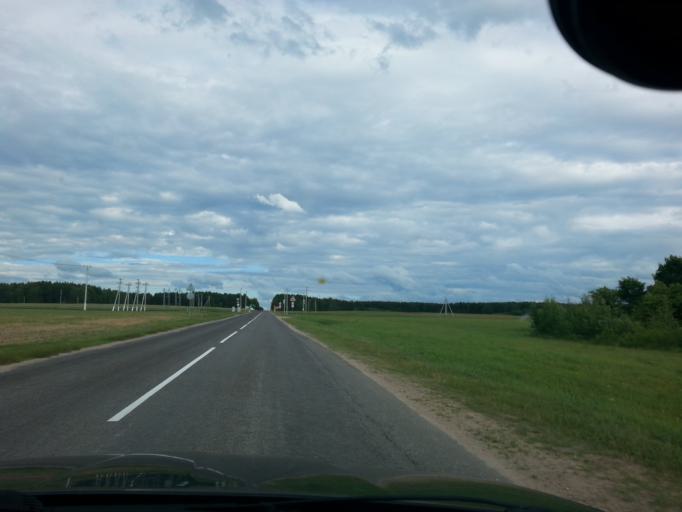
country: BY
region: Grodnenskaya
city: Astravyets
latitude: 54.7100
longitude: 26.0833
